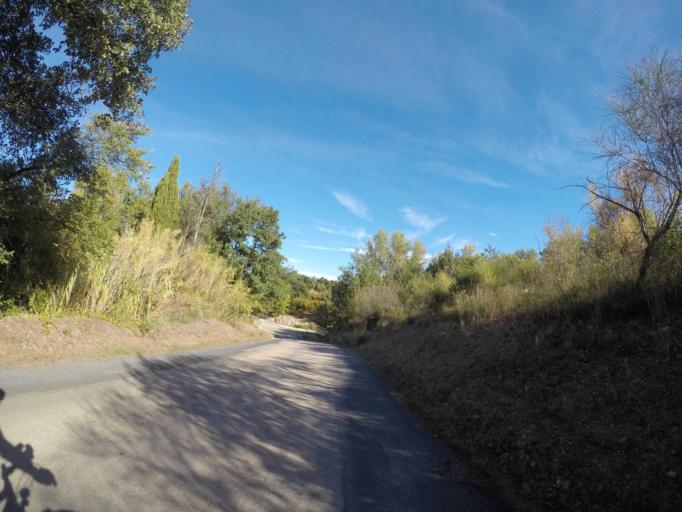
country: FR
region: Languedoc-Roussillon
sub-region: Departement des Pyrenees-Orientales
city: Trouillas
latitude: 42.5867
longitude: 2.8098
